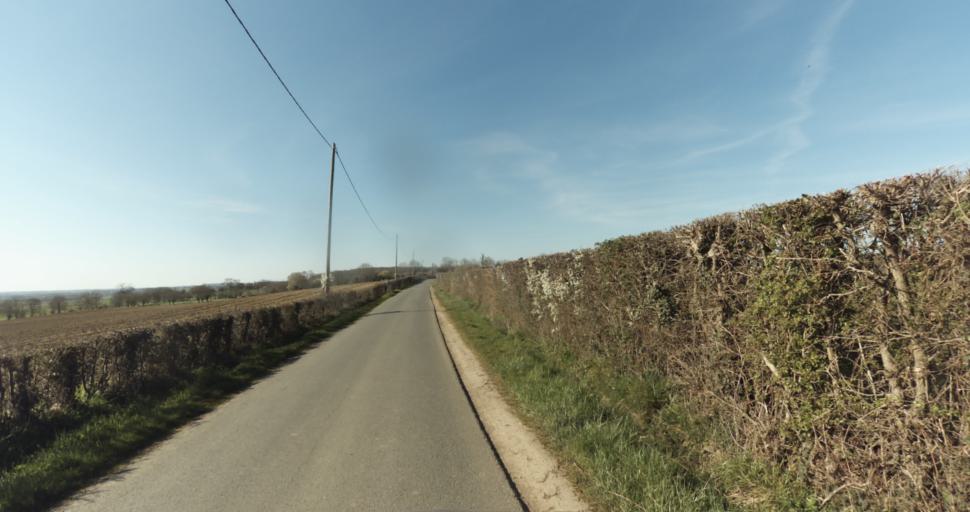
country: FR
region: Lower Normandy
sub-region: Departement du Calvados
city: Saint-Pierre-sur-Dives
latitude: 49.0313
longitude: 0.0570
